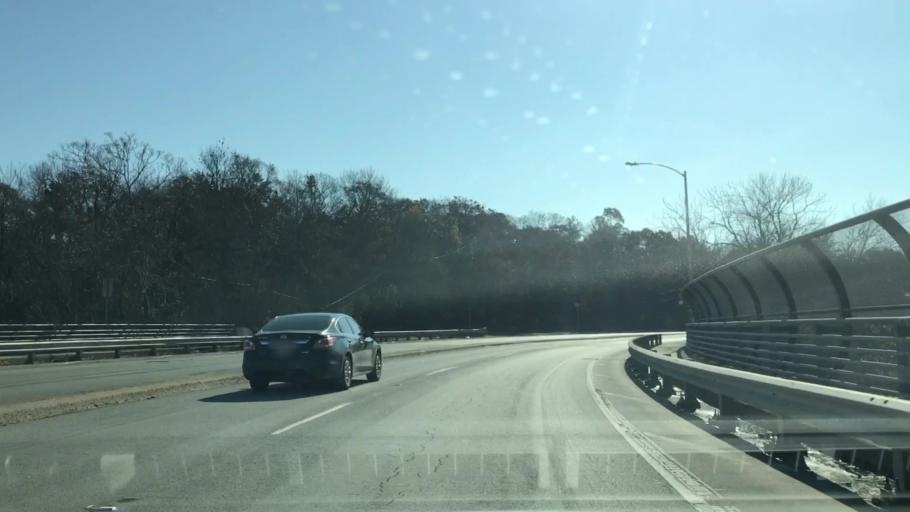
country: US
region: Texas
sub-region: Dallas County
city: Dallas
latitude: 32.7397
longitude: -96.8132
